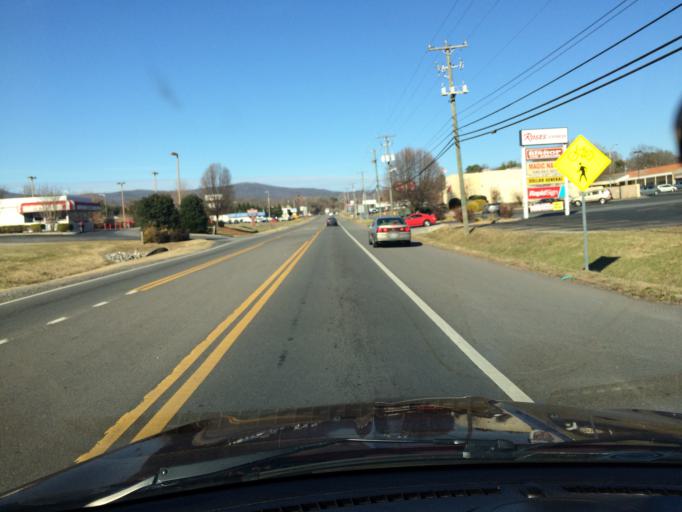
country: US
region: Virginia
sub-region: Roanoke County
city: Hollins
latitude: 37.3344
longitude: -79.9549
